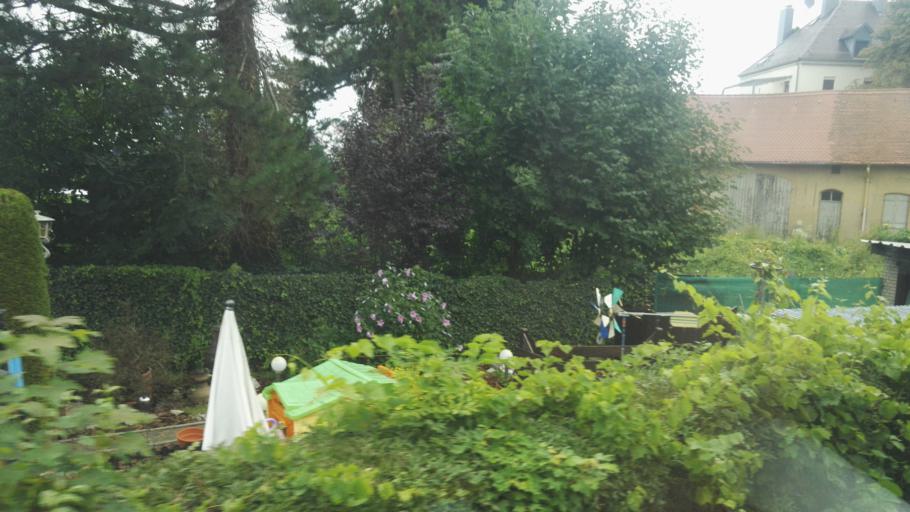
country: DE
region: Bavaria
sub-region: Swabia
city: Augsburg
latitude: 48.3866
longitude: 10.8879
